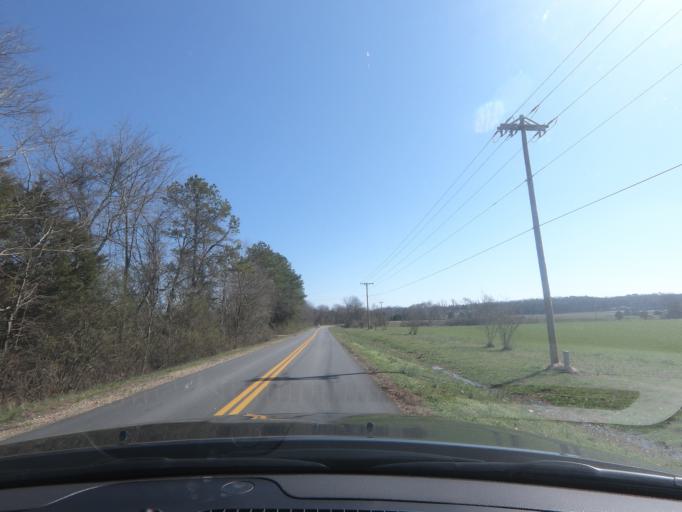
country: US
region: Georgia
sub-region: Gordon County
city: Calhoun
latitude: 34.4617
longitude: -84.9873
